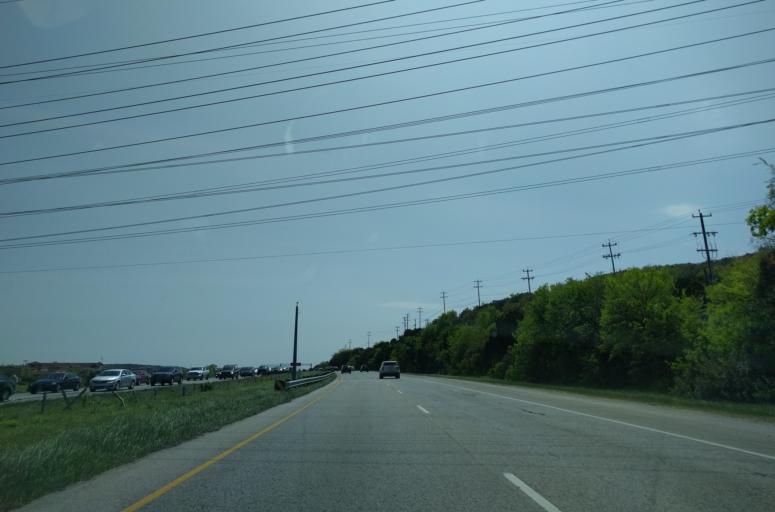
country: US
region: Texas
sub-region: Bexar County
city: Cross Mountain
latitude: 29.6171
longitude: -98.6071
